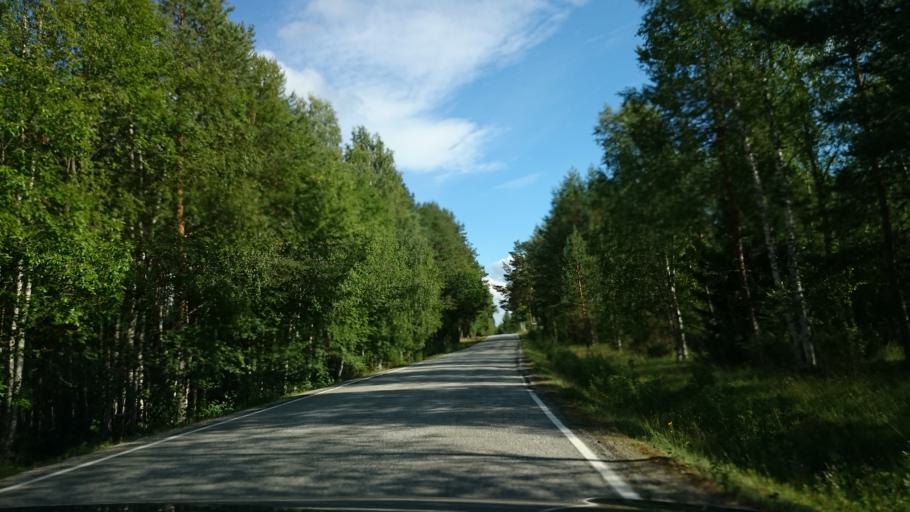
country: FI
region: Kainuu
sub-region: Kehys-Kainuu
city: Suomussalmi
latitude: 64.7604
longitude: 29.3840
